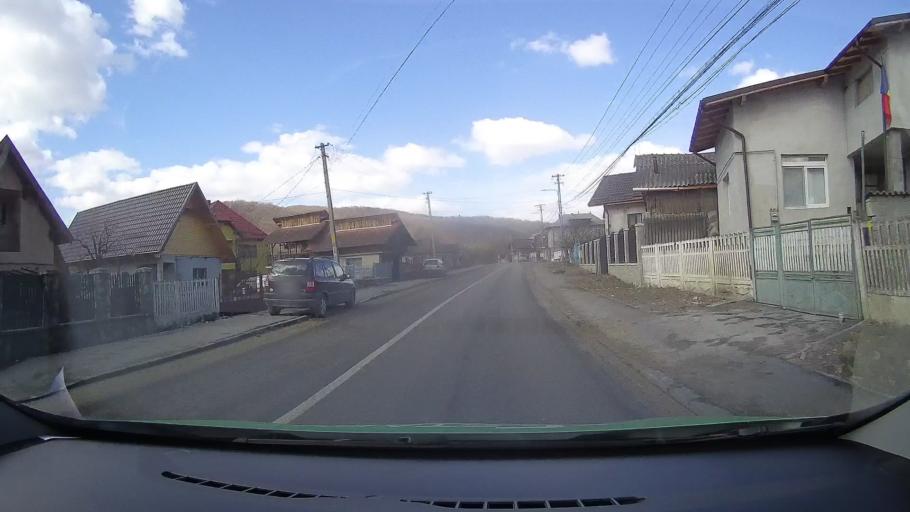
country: RO
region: Dambovita
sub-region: Comuna Fieni
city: Fieni
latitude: 45.1310
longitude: 25.4072
